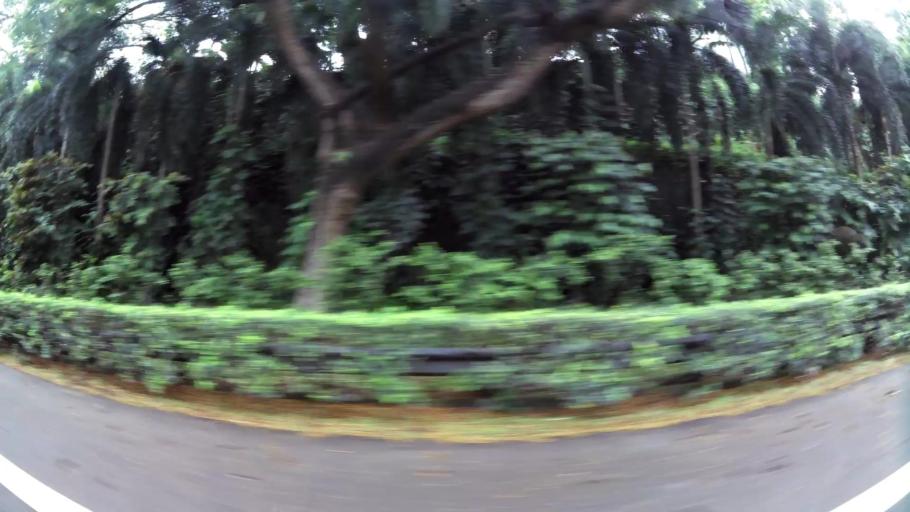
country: SG
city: Singapore
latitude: 1.2798
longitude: 103.8185
